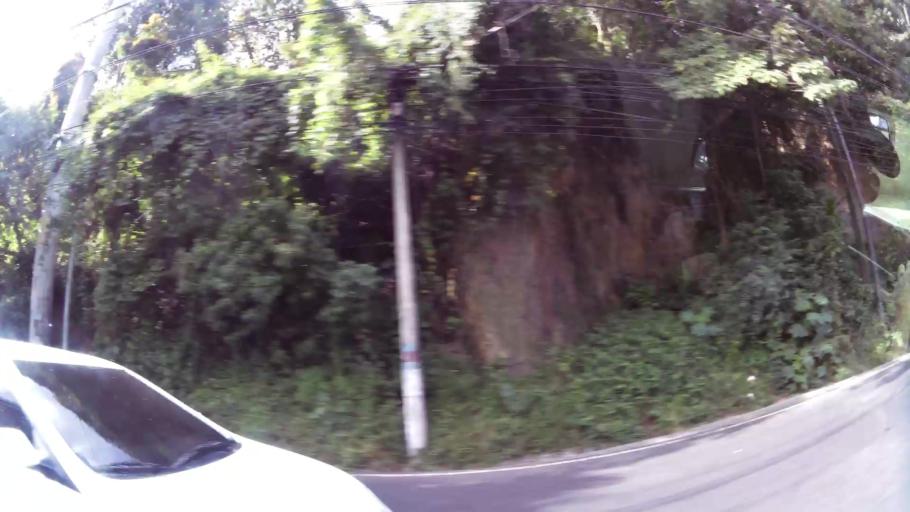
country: GT
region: Guatemala
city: Santa Catarina Pinula
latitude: 14.5718
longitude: -90.4880
